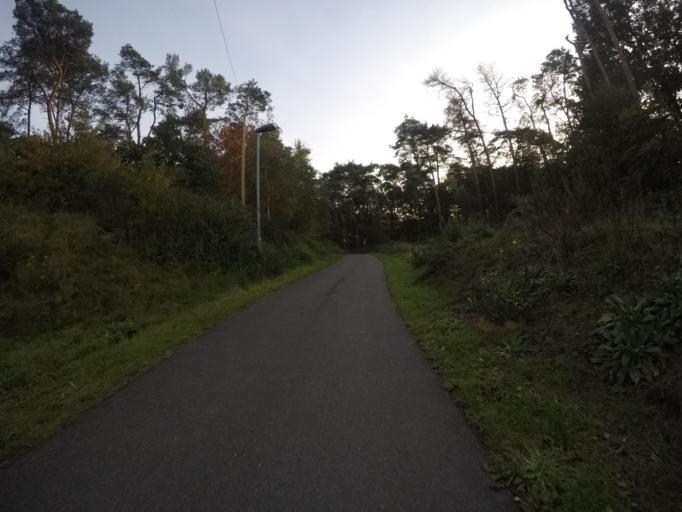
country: DE
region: North Rhine-Westphalia
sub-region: Regierungsbezirk Munster
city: Rhede
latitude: 51.8256
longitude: 6.6873
